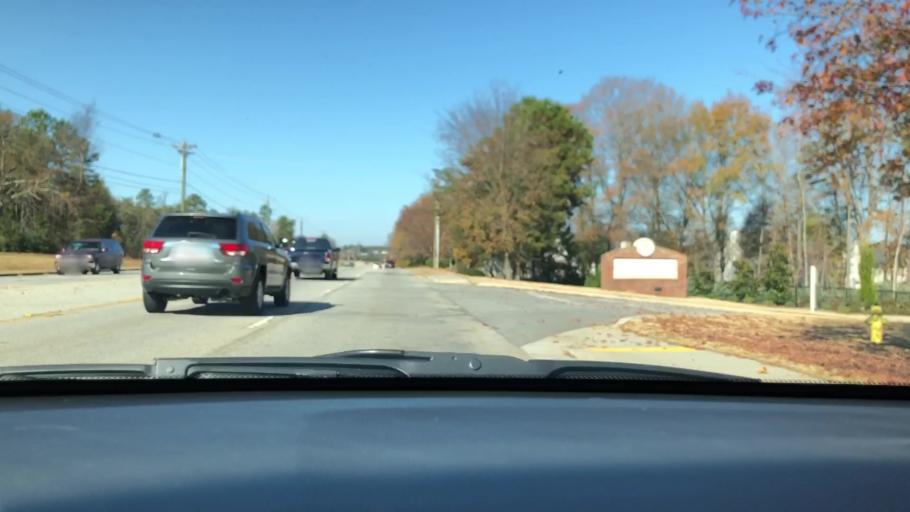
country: US
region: South Carolina
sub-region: Greenville County
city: Five Forks
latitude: 34.8150
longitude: -82.2462
